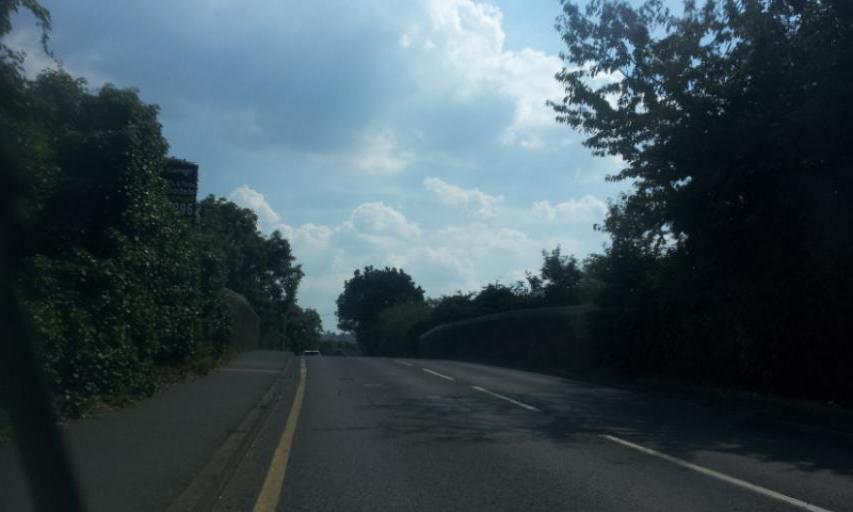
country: GB
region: England
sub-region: Kent
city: Paddock Wood
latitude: 51.1830
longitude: 0.3870
